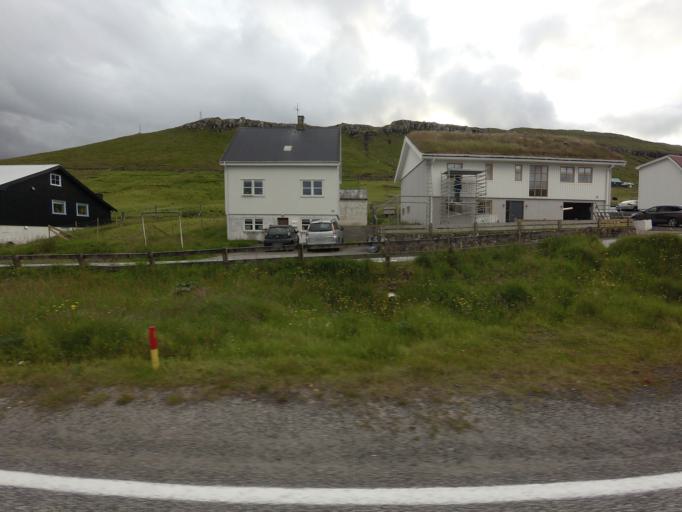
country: FO
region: Streymoy
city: Kollafjordhur
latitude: 62.1235
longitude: -6.8744
